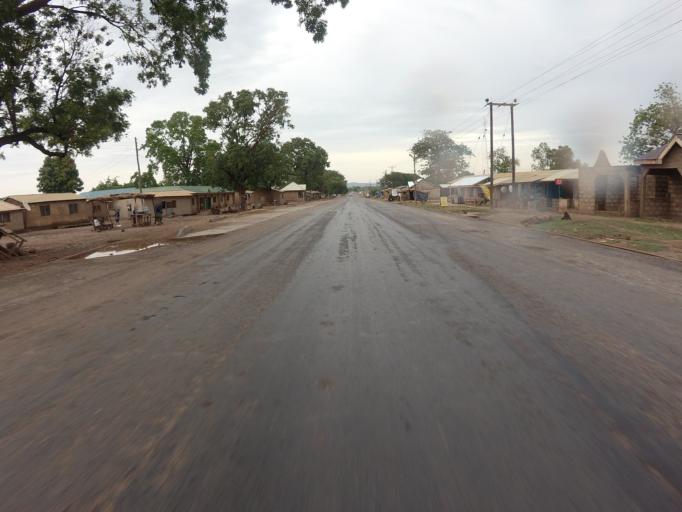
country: GH
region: Upper East
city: Bolgatanga
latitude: 10.8590
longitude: -0.6650
